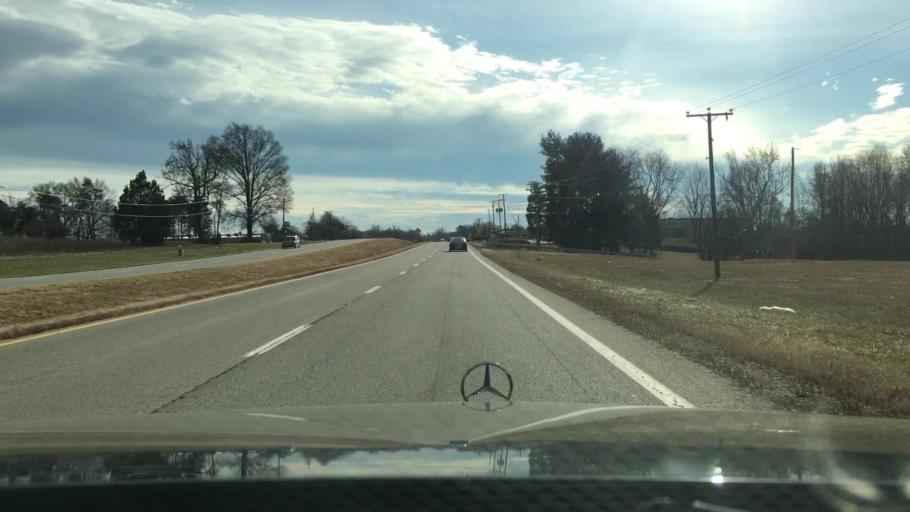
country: US
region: Virginia
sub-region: Pittsylvania County
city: Mount Hermon
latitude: 36.7370
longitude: -79.3805
